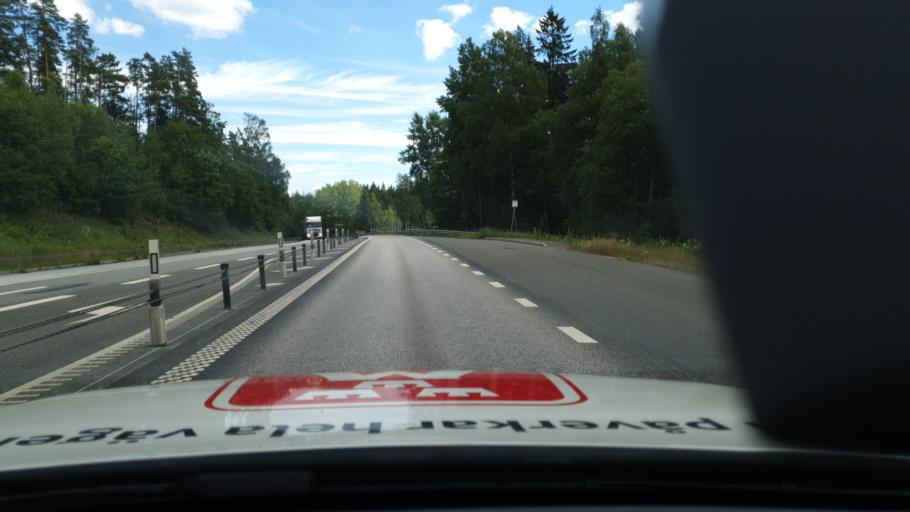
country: SE
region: Joenkoeping
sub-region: Jonkopings Kommun
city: Huskvarna
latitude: 57.7557
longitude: 14.2576
